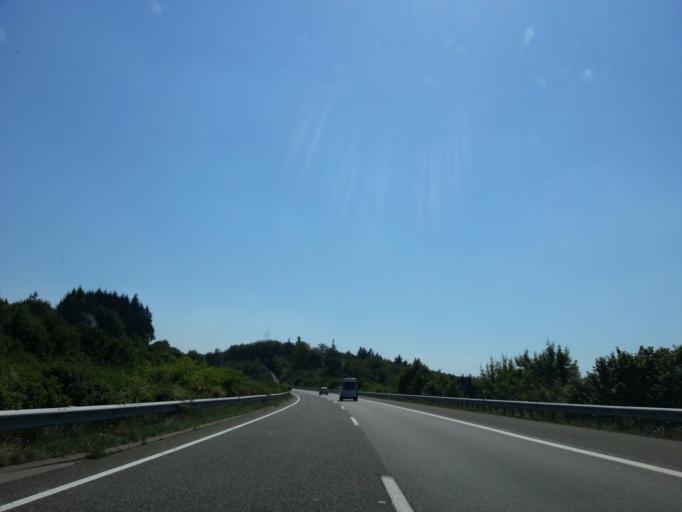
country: DE
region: Rheinland-Pfalz
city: Etteldorf
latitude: 50.0237
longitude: 6.5562
